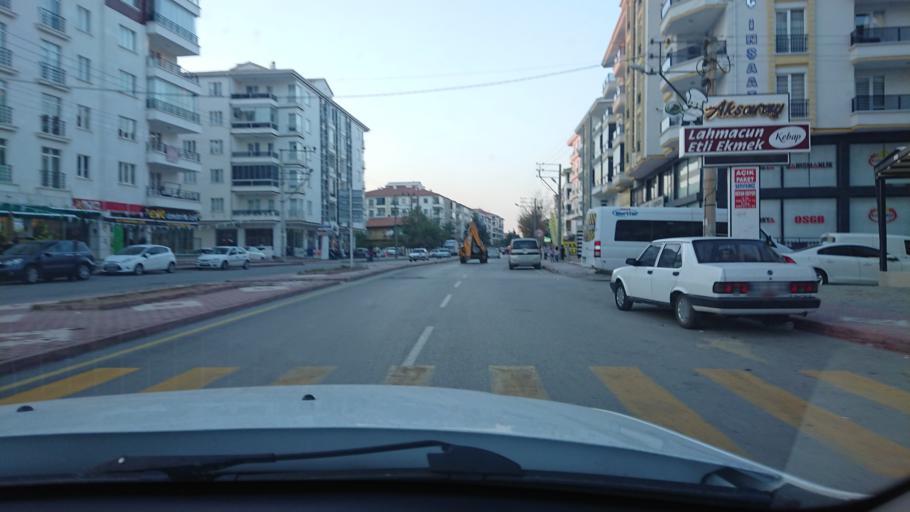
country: TR
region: Aksaray
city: Aksaray
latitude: 38.3595
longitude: 34.0387
